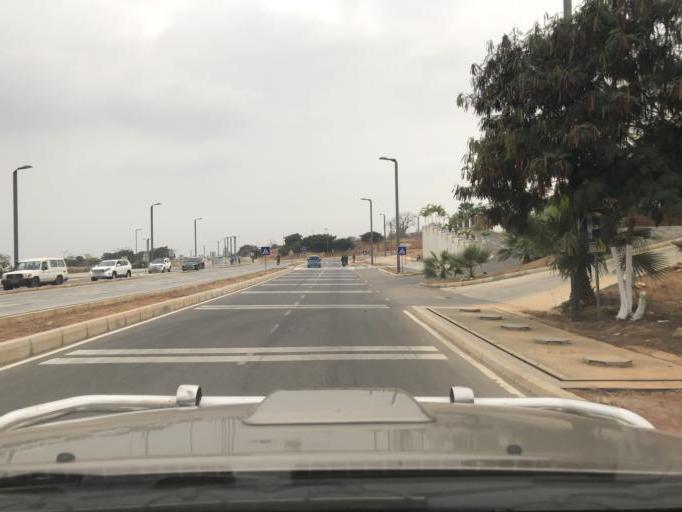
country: AO
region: Luanda
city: Luanda
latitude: -8.8998
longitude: 13.1749
